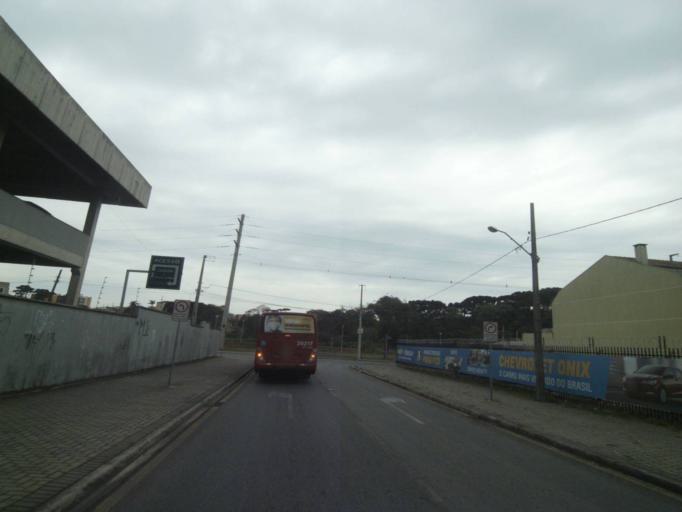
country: BR
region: Parana
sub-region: Sao Jose Dos Pinhais
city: Sao Jose dos Pinhais
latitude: -25.5177
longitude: -49.1992
